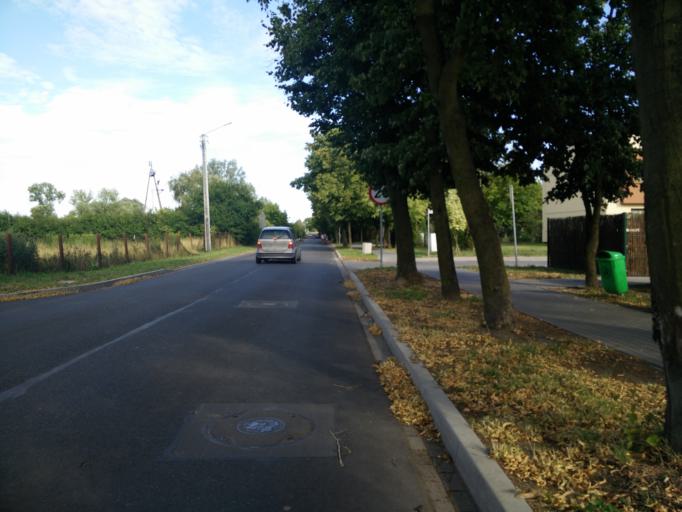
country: PL
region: Greater Poland Voivodeship
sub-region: Powiat sredzki
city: Sroda Wielkopolska
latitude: 52.2344
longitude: 17.2596
